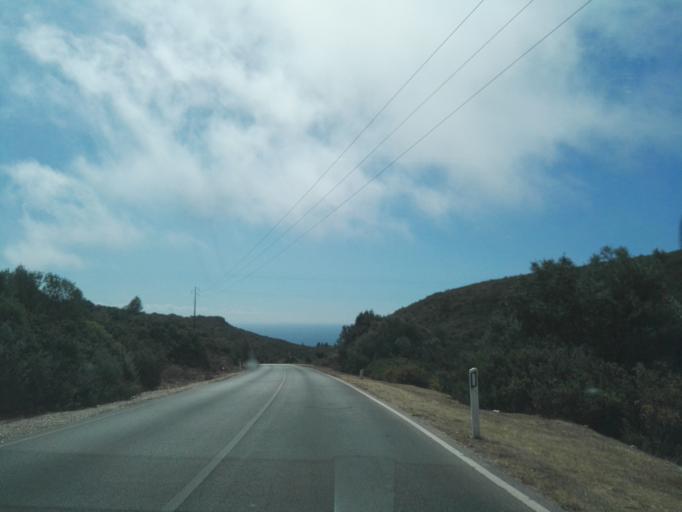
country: PT
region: Setubal
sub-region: Sesimbra
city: Sesimbra
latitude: 38.4456
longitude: -9.0871
